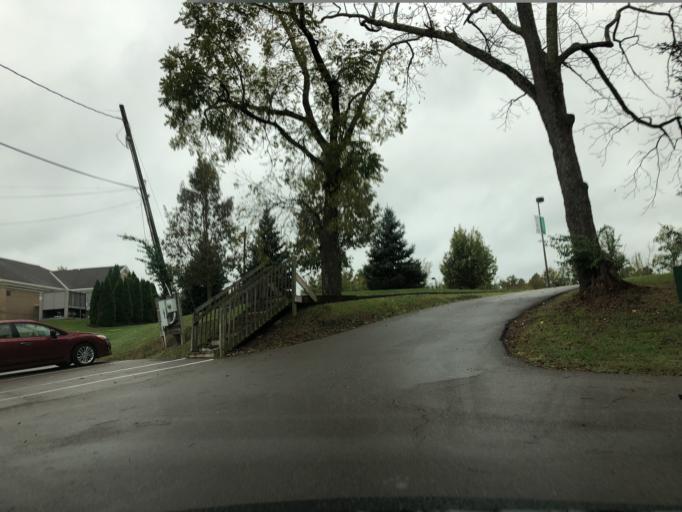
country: US
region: Ohio
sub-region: Hamilton County
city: Loveland
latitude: 39.2598
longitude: -84.2468
